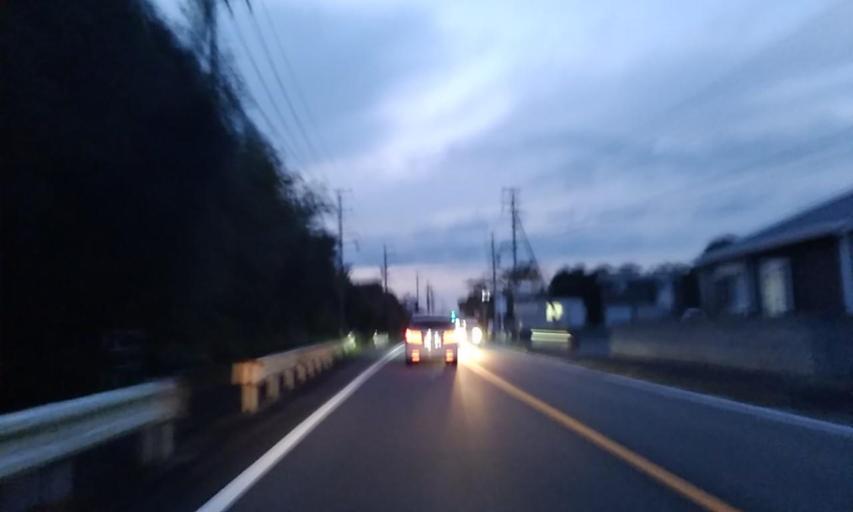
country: JP
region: Mie
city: Toba
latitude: 34.3098
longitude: 136.8686
